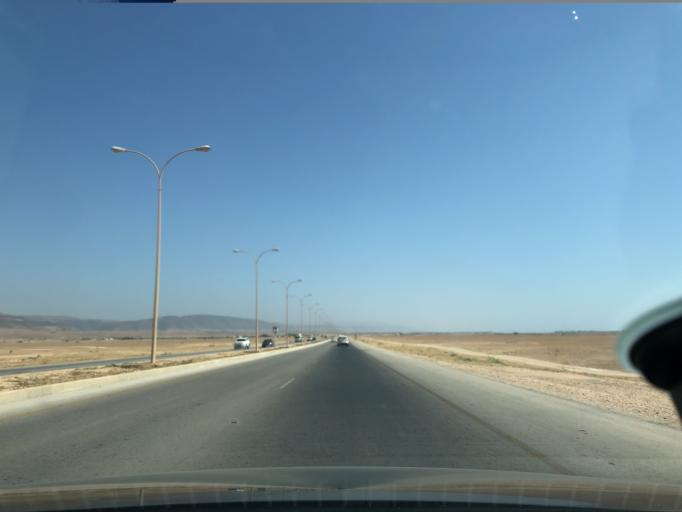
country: OM
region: Zufar
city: Salalah
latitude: 17.0512
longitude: 54.2566
